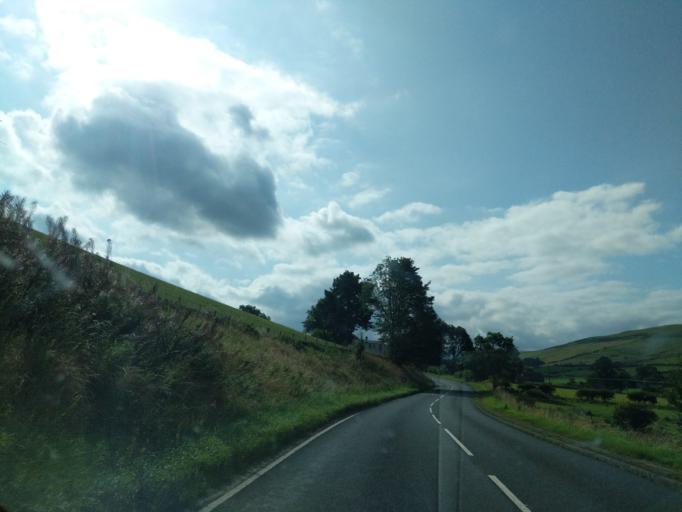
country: GB
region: Scotland
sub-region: The Scottish Borders
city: Peebles
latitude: 55.6859
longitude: -3.2112
